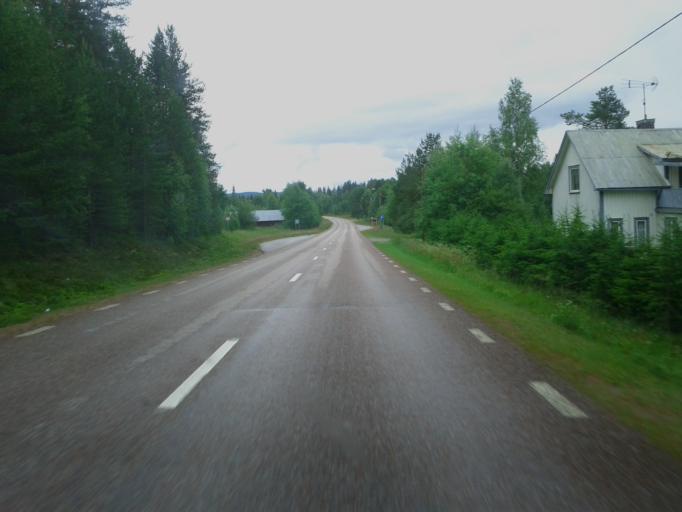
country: NO
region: Hedmark
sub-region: Trysil
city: Innbygda
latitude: 61.7263
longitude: 12.9928
